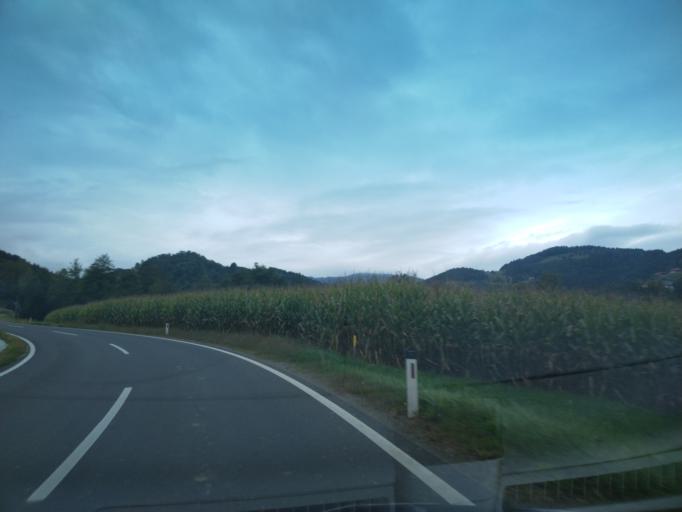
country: AT
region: Styria
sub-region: Politischer Bezirk Deutschlandsberg
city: Wernersdorf
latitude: 46.7177
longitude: 15.2311
